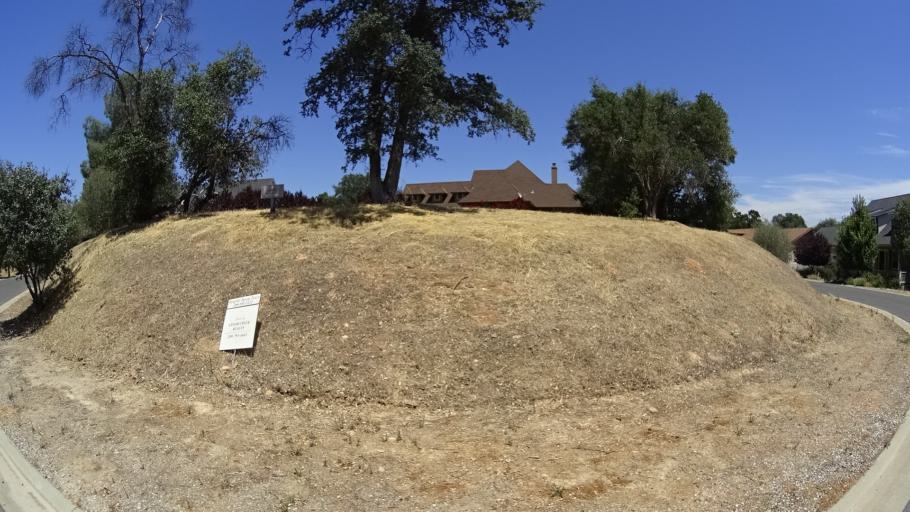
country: US
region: California
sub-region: Calaveras County
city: Angels Camp
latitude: 38.0656
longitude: -120.5649
